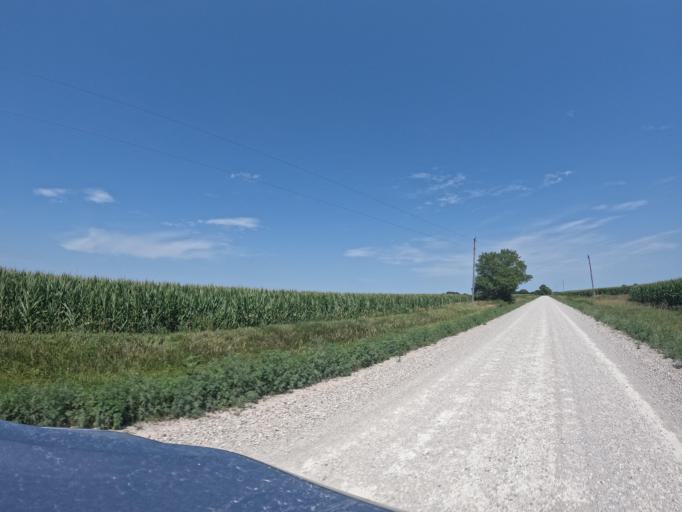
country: US
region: Iowa
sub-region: Henry County
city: Mount Pleasant
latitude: 40.8901
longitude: -91.6375
